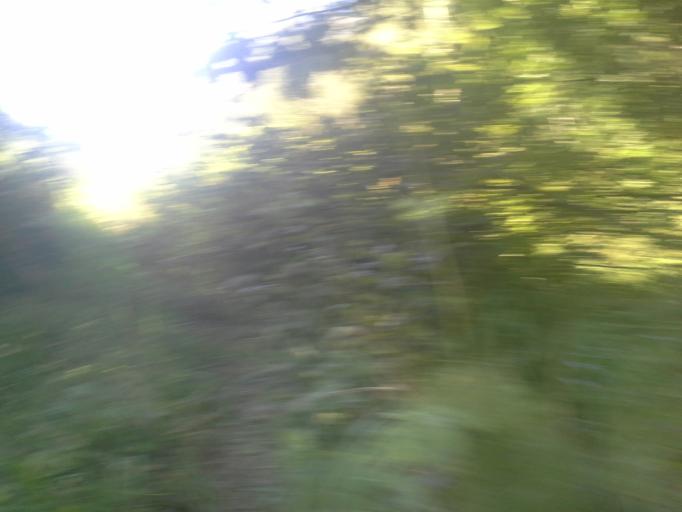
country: RU
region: Moskovskaya
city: Kievskij
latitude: 55.3467
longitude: 36.9376
